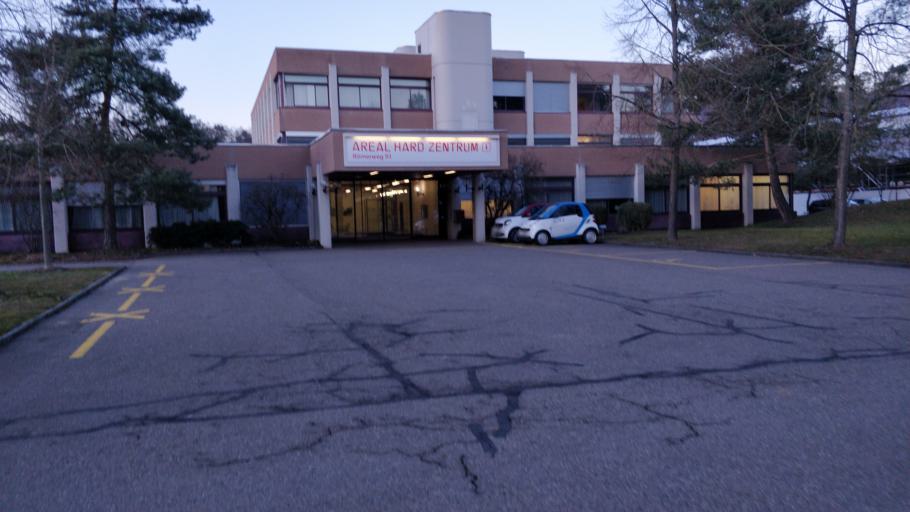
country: CH
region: Zurich
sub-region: Bezirk Buelach
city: Freienstein
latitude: 47.5239
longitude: 8.5849
